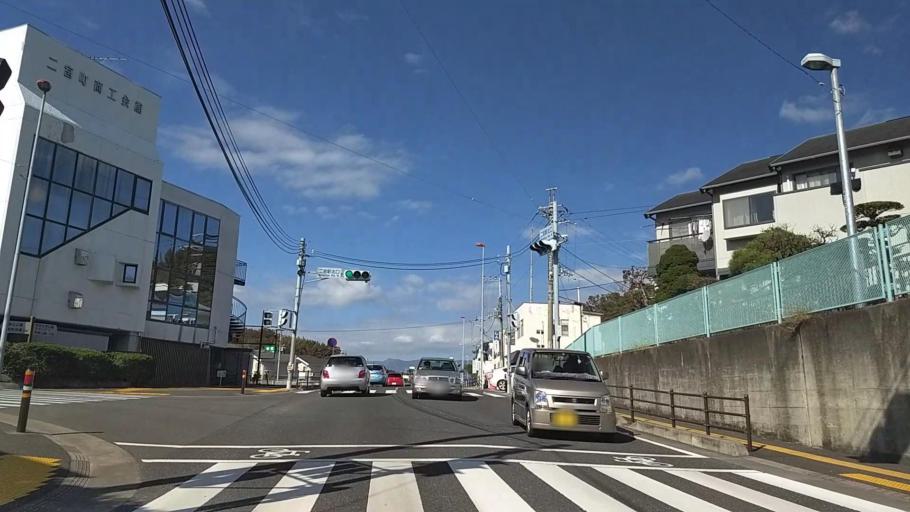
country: JP
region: Kanagawa
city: Ninomiya
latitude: 35.3006
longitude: 139.2597
